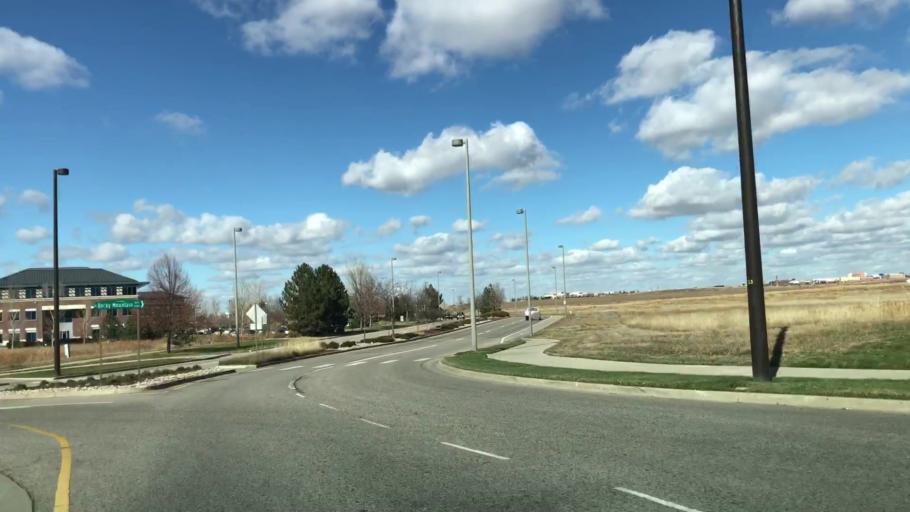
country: US
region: Colorado
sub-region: Larimer County
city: Loveland
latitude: 40.4175
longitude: -104.9999
